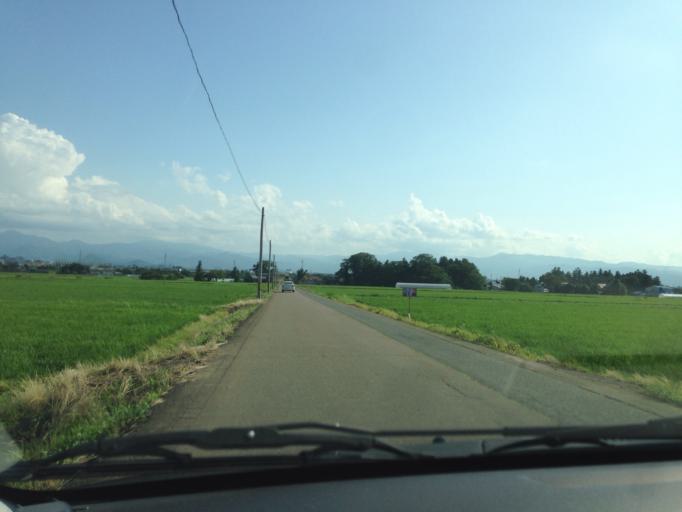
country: JP
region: Fukushima
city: Kitakata
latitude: 37.5367
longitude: 139.9379
